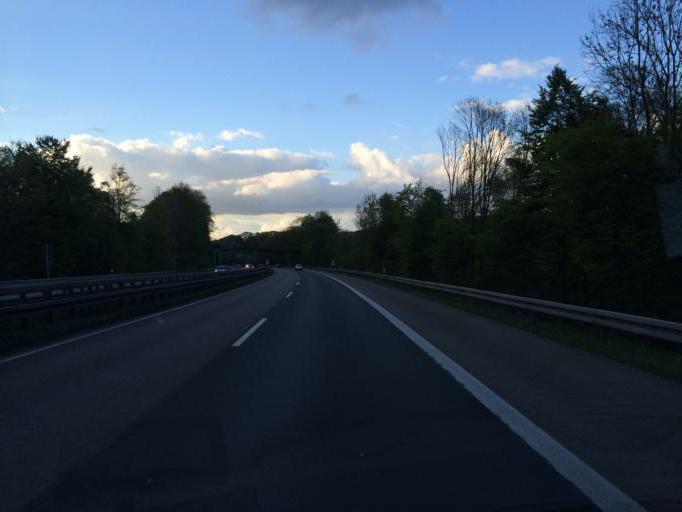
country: DE
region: North Rhine-Westphalia
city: Sprockhovel
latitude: 51.3659
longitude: 7.2756
